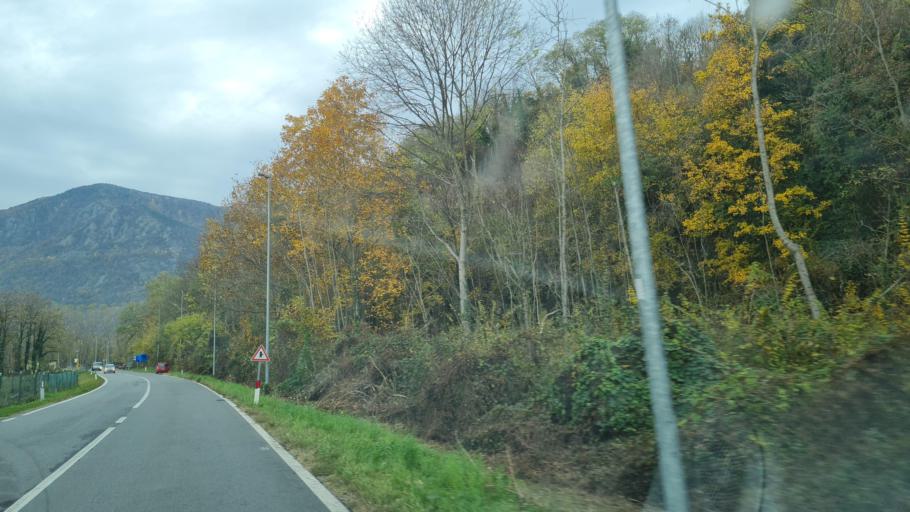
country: IT
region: Piedmont
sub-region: Provincia di Torino
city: Villar Dora
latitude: 45.1055
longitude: 7.3759
